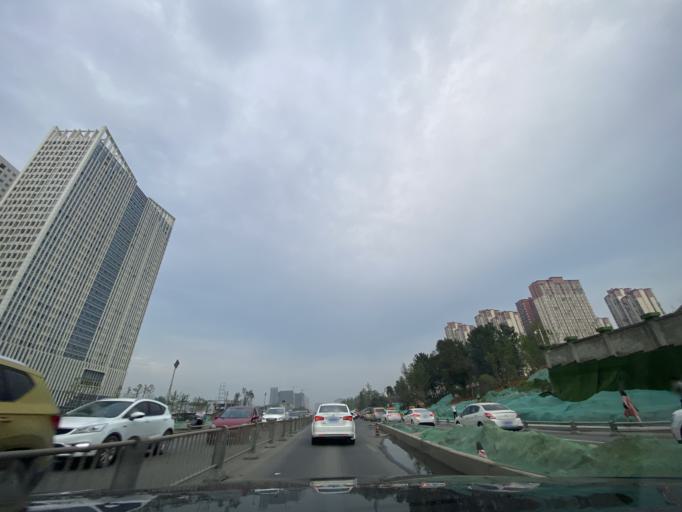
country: CN
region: Sichuan
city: Longquan
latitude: 30.6502
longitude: 104.2227
